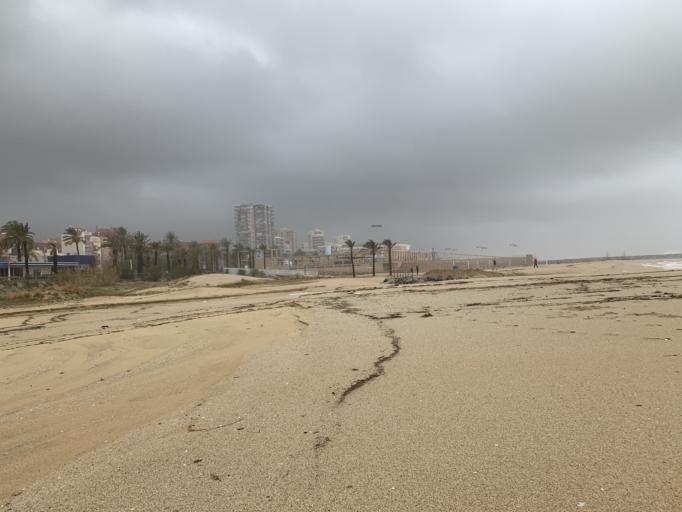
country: ES
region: Catalonia
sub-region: Provincia de Barcelona
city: Mataro
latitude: 41.5361
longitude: 2.4513
